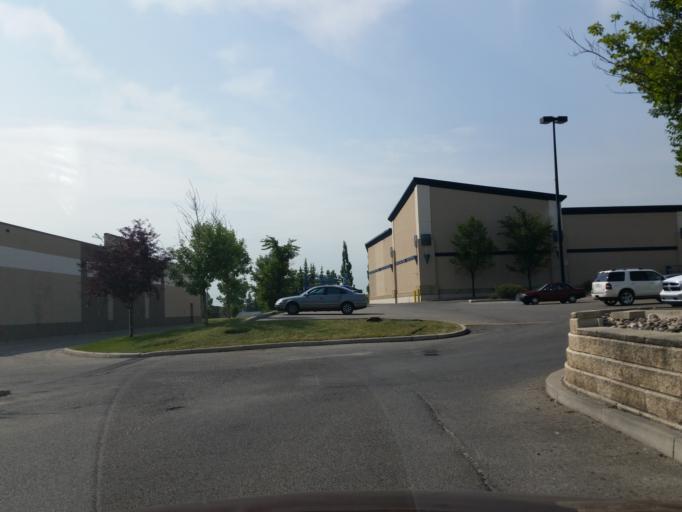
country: CA
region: Alberta
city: Calgary
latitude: 51.0686
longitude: -113.9895
